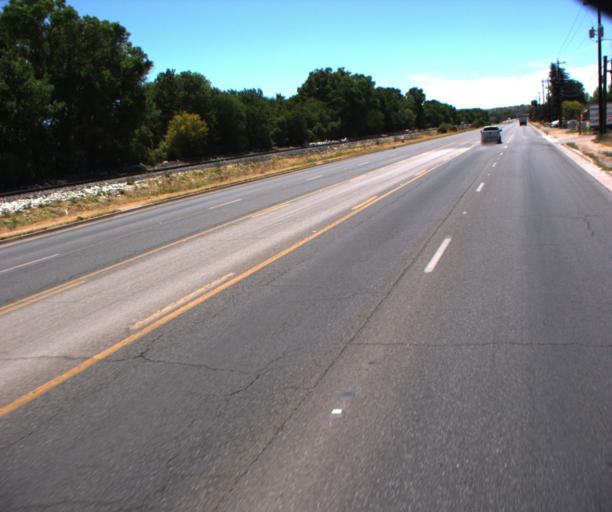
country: US
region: Arizona
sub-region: Santa Cruz County
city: Nogales
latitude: 31.3770
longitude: -110.9391
